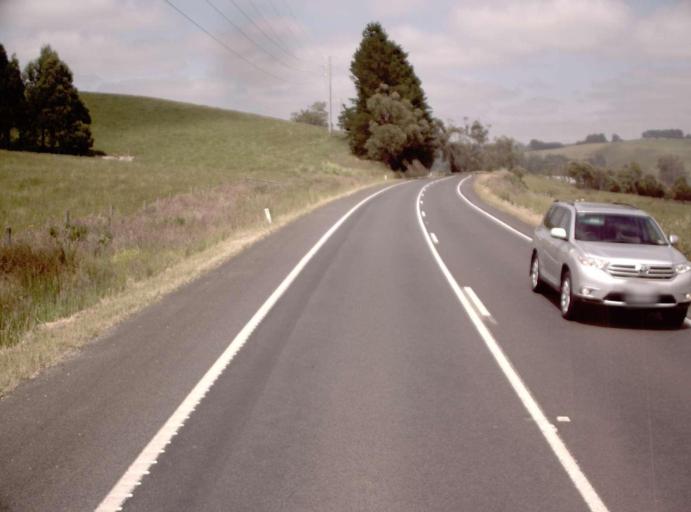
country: AU
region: Victoria
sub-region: Baw Baw
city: Warragul
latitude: -38.4110
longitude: 146.0483
